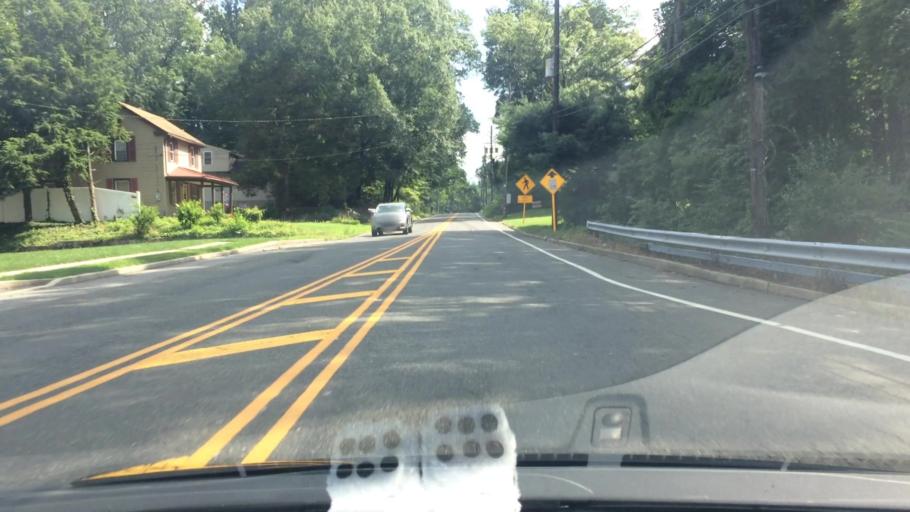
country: US
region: New Jersey
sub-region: Camden County
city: Glendora
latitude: 39.8239
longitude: -75.0996
